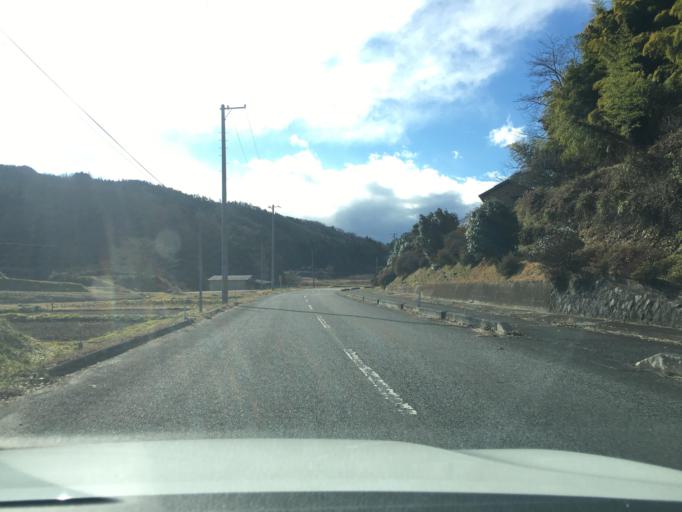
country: JP
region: Fukushima
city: Funehikimachi-funehiki
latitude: 37.3695
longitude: 140.6304
